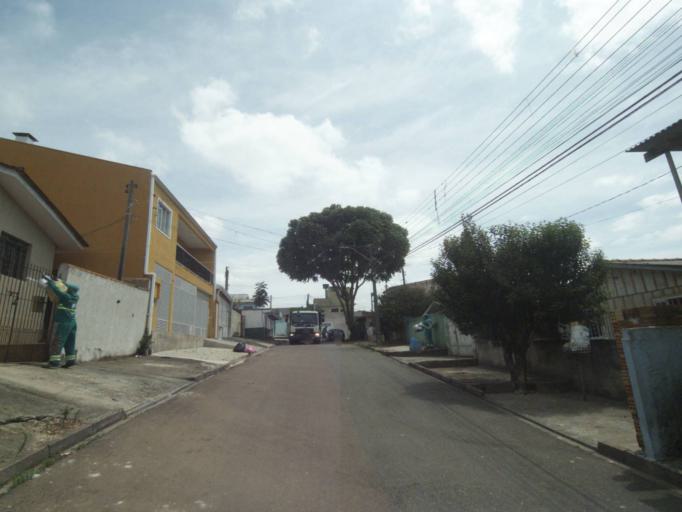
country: BR
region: Parana
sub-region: Curitiba
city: Curitiba
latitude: -25.4928
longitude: -49.3406
